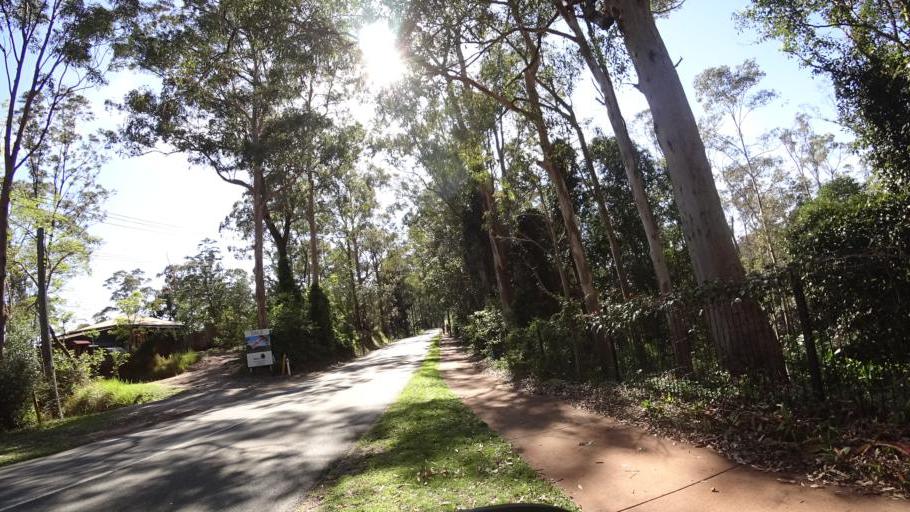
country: AU
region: Queensland
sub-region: Moreton Bay
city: Highvale
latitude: -27.3990
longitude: 152.7861
